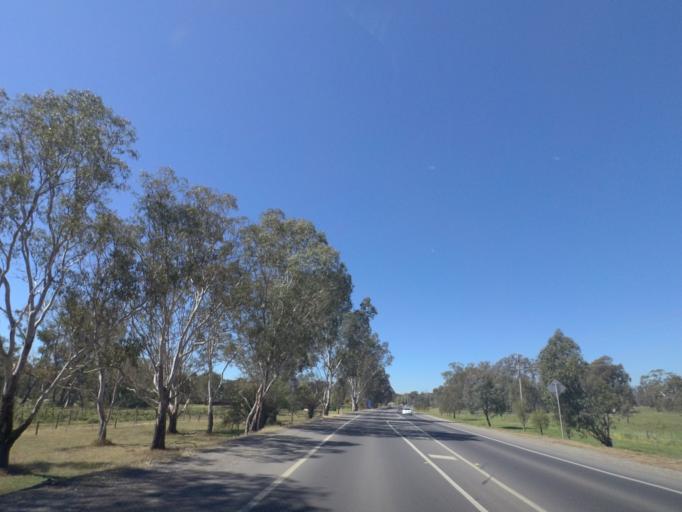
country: AU
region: Victoria
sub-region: Murrindindi
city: Kinglake West
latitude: -37.0242
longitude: 145.1129
